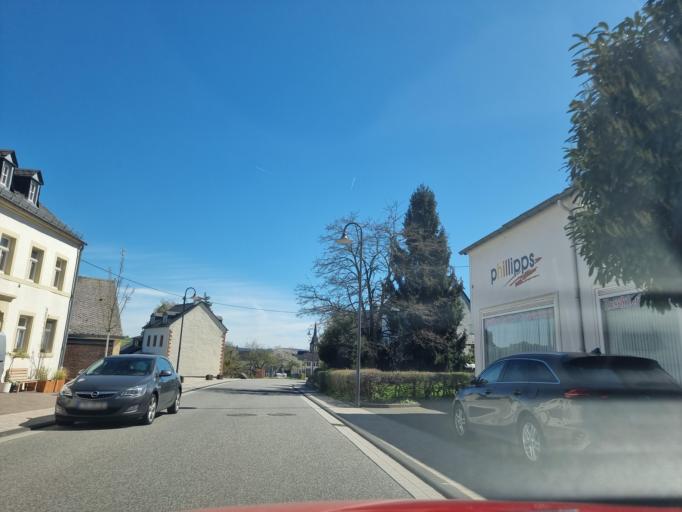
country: DE
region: Rheinland-Pfalz
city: Welschbillig
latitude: 49.8535
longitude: 6.5616
